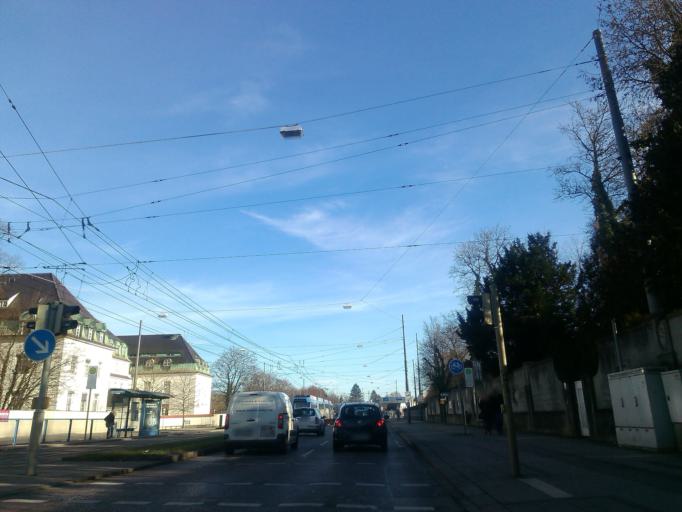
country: DE
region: Bavaria
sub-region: Upper Bavaria
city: Pasing
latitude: 48.1644
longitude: 11.5026
